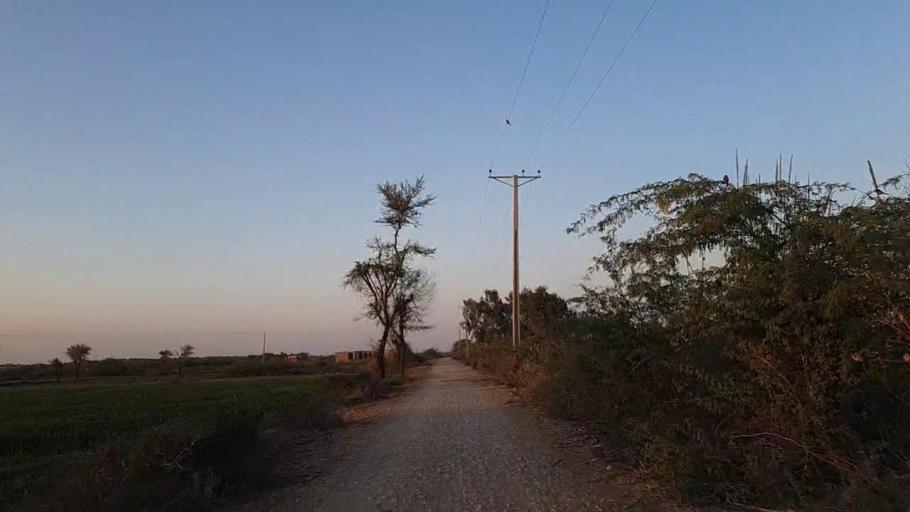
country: PK
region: Sindh
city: Jam Sahib
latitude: 26.3125
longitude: 68.6536
